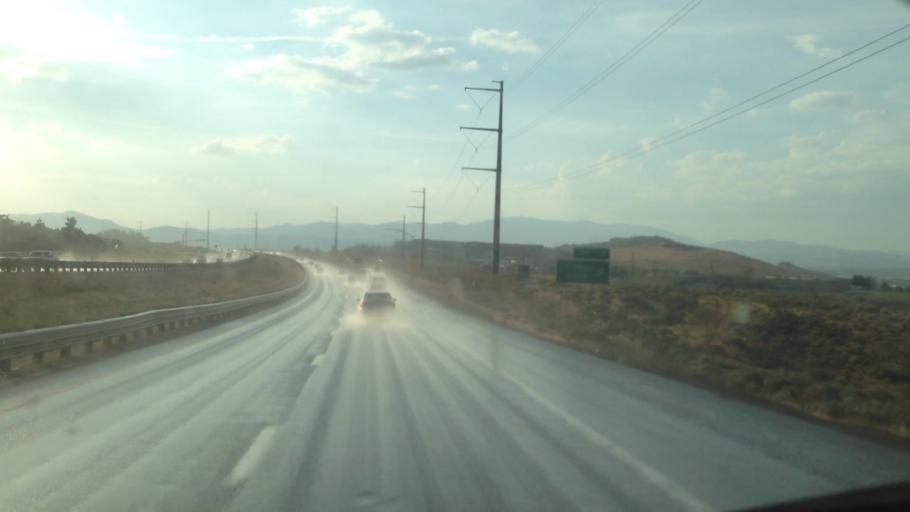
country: US
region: Nevada
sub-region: Washoe County
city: Golden Valley
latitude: 39.6072
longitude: -119.8451
